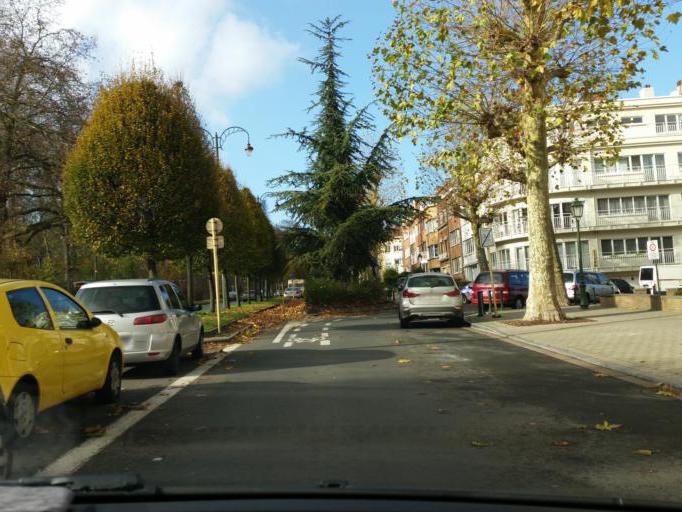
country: BE
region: Flanders
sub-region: Provincie Vlaams-Brabant
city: Grimbergen
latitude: 50.8923
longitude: 4.3667
